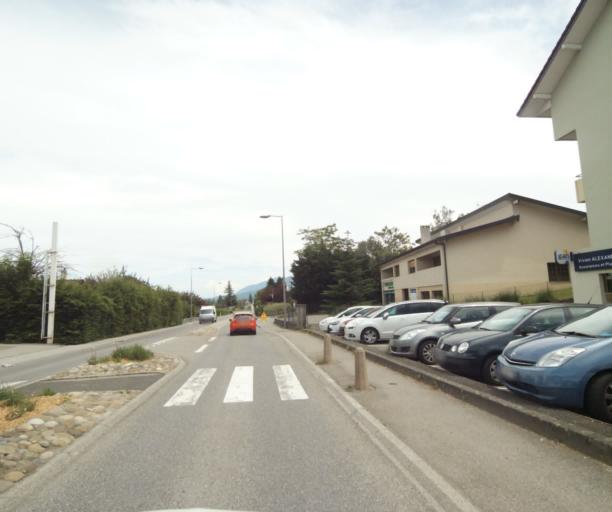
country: FR
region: Rhone-Alpes
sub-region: Departement de la Haute-Savoie
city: Bons-en-Chablais
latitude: 46.2664
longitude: 6.3752
